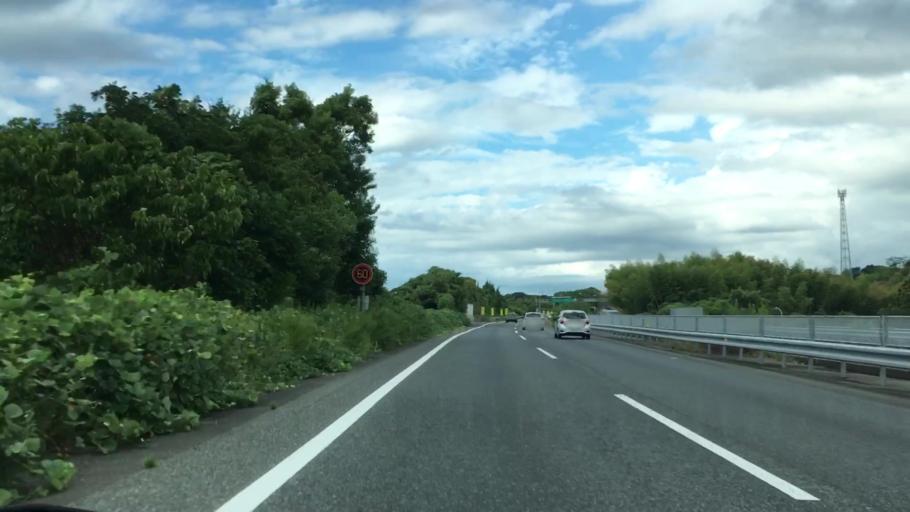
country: JP
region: Fukuoka
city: Maebaru-chuo
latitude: 33.5385
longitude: 130.1969
